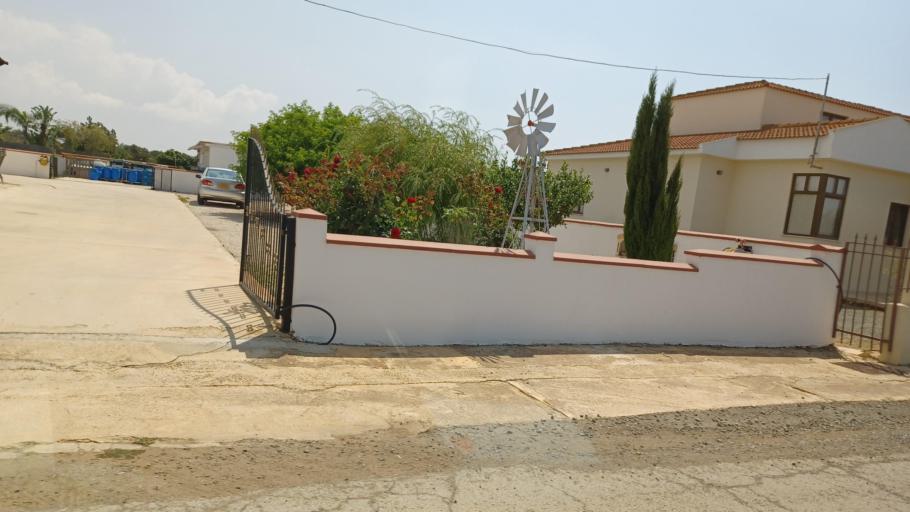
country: CY
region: Ammochostos
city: Liopetri
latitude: 34.9891
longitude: 33.8589
